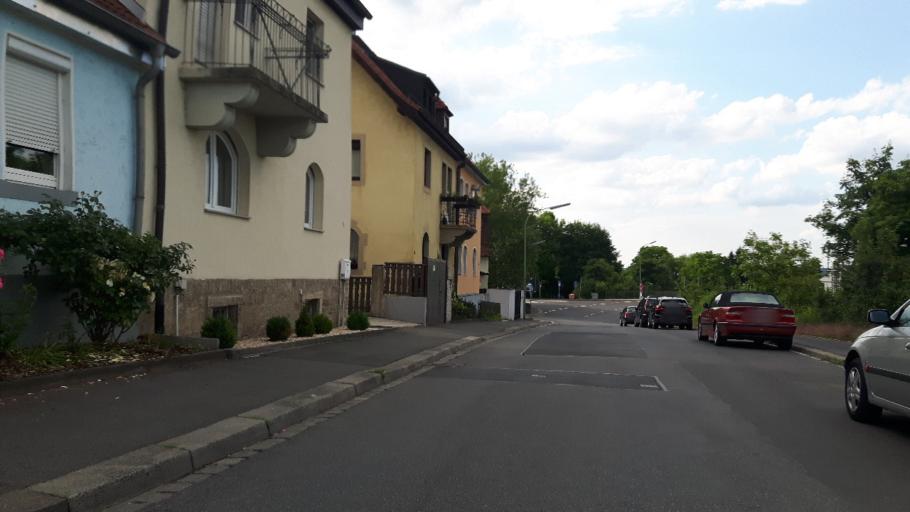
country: DE
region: Bavaria
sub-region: Regierungsbezirk Unterfranken
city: Wuerzburg
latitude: 49.7625
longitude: 9.9420
